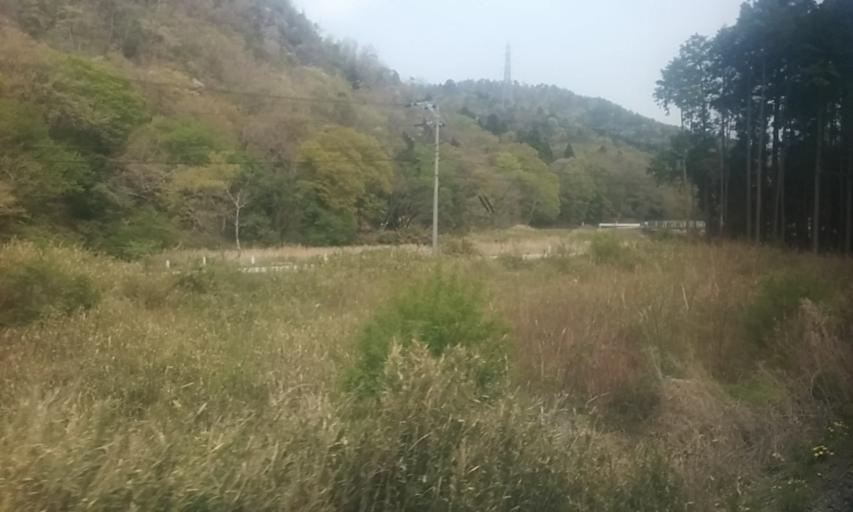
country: JP
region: Shiga Prefecture
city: Nagahama
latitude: 35.3423
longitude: 136.3625
